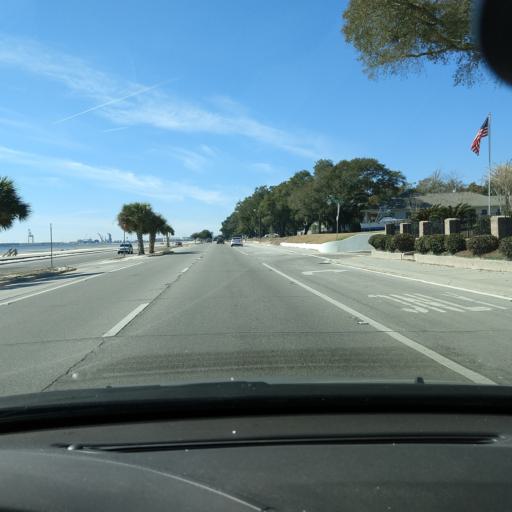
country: US
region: Mississippi
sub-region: Harrison County
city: Gulfport
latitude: 30.3731
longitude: -89.0686
